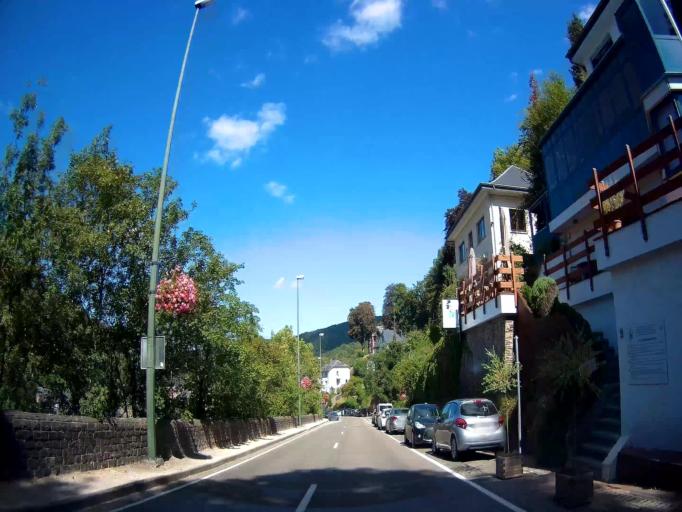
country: BE
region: Wallonia
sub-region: Province du Luxembourg
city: La Roche-en-Ardenne
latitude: 50.1778
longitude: 5.5775
